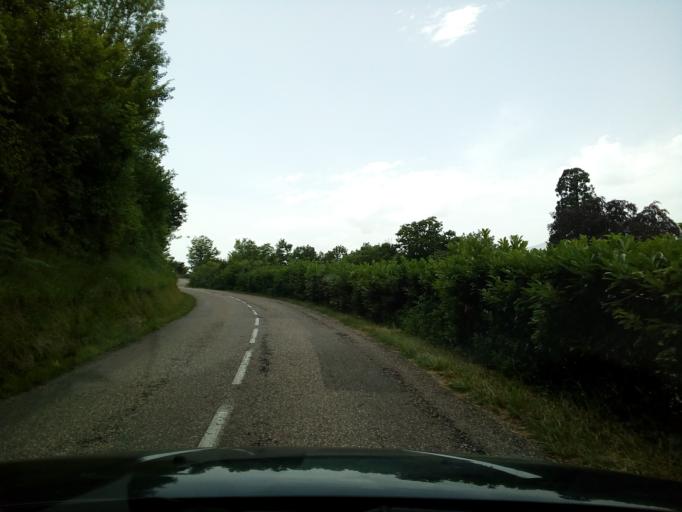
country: FR
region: Rhone-Alpes
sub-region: Departement de l'Isere
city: Saint-Martin-d'Heres
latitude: 45.1704
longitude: 5.7735
